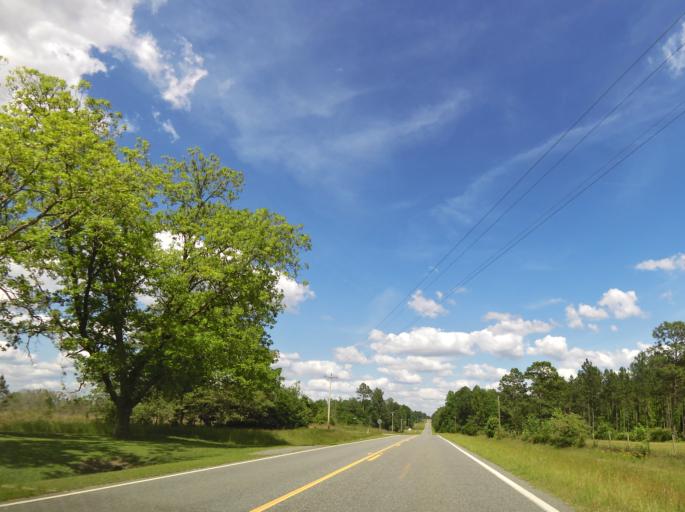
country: US
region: Georgia
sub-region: Wheeler County
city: Alamo
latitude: 32.2492
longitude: -82.9193
